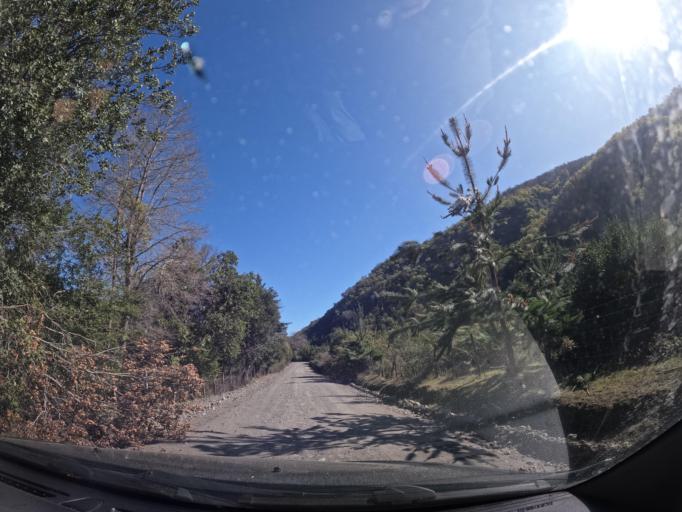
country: CL
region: Maule
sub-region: Provincia de Linares
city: Longavi
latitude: -36.2283
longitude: -71.3952
